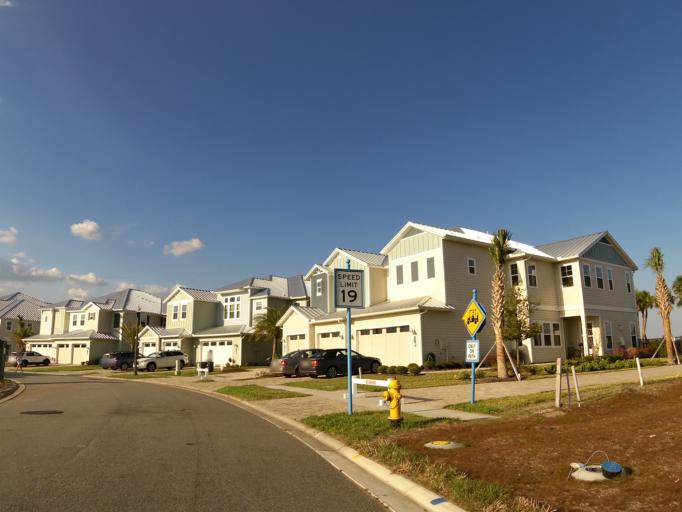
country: US
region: Florida
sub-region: Saint Johns County
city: Palm Valley
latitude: 30.0804
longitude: -81.4837
